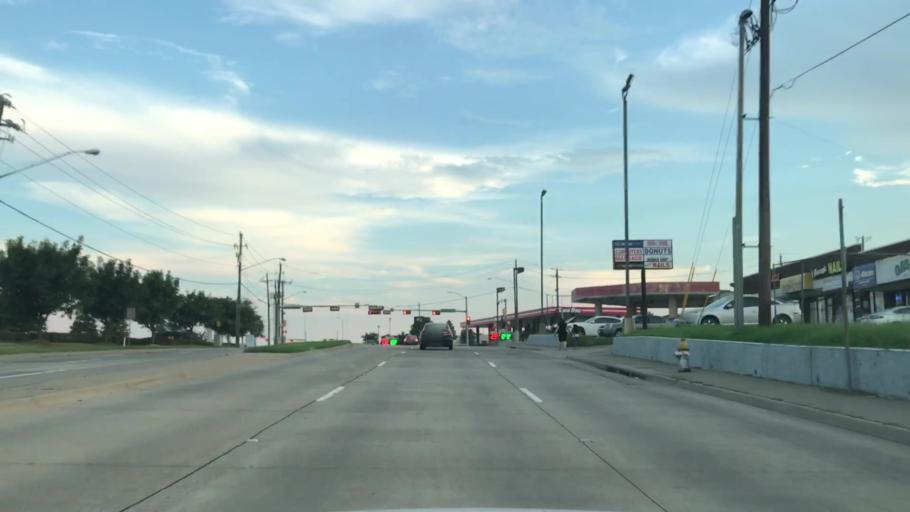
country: US
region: Texas
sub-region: Dallas County
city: Addison
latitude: 33.0043
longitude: -96.8574
